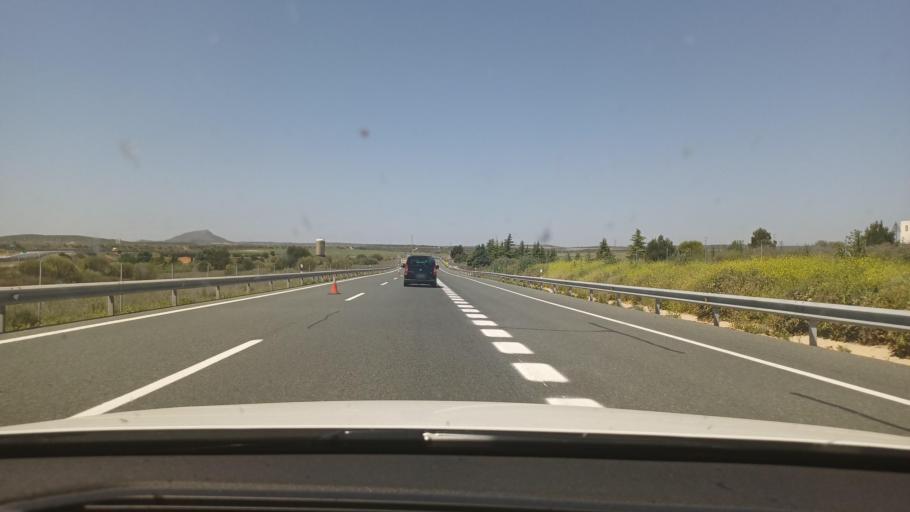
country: ES
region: Castille-La Mancha
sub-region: Provincia de Albacete
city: Alpera
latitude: 38.8789
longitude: -1.2228
